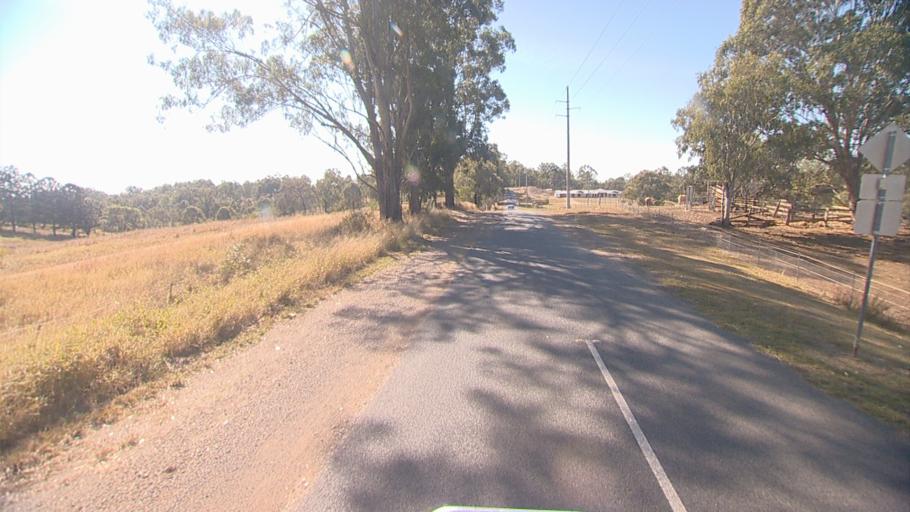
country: AU
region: Queensland
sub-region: Logan
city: Cedar Vale
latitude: -27.8953
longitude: 153.0148
